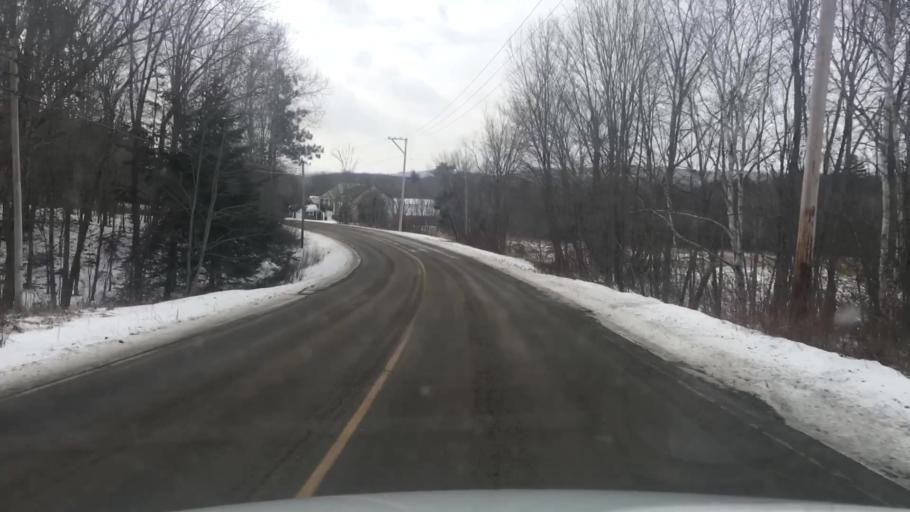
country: US
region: Maine
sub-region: Knox County
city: Hope
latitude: 44.2907
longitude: -69.0892
